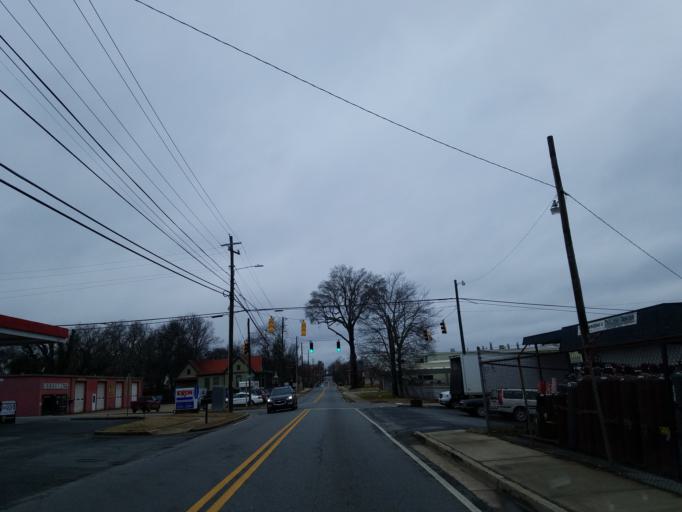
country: US
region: Georgia
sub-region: Bartow County
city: Cartersville
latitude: 34.1612
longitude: -84.7953
